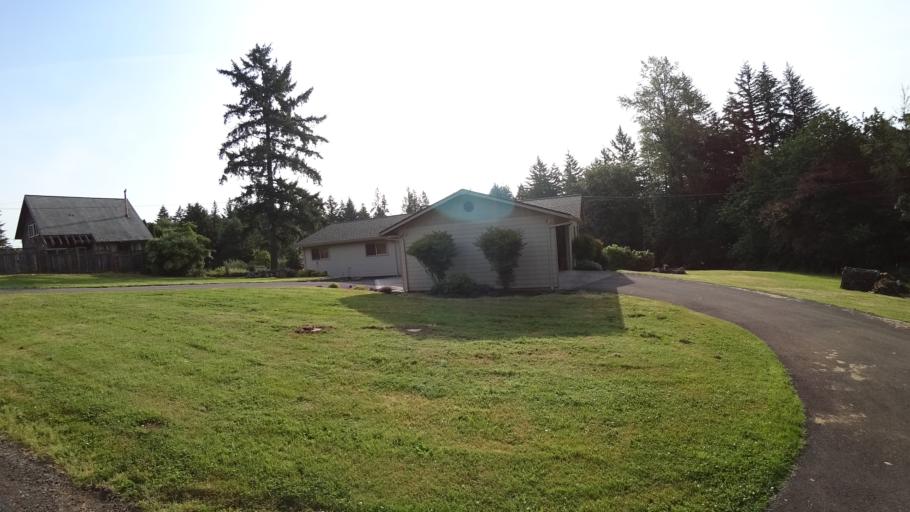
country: US
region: Oregon
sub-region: Clackamas County
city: Happy Valley
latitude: 45.4580
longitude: -122.5069
